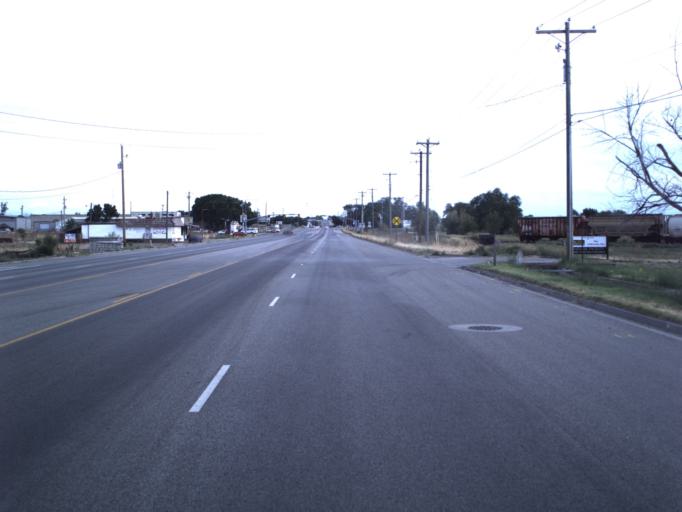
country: US
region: Utah
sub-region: Weber County
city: Marriott-Slaterville
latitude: 41.2315
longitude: -112.0257
